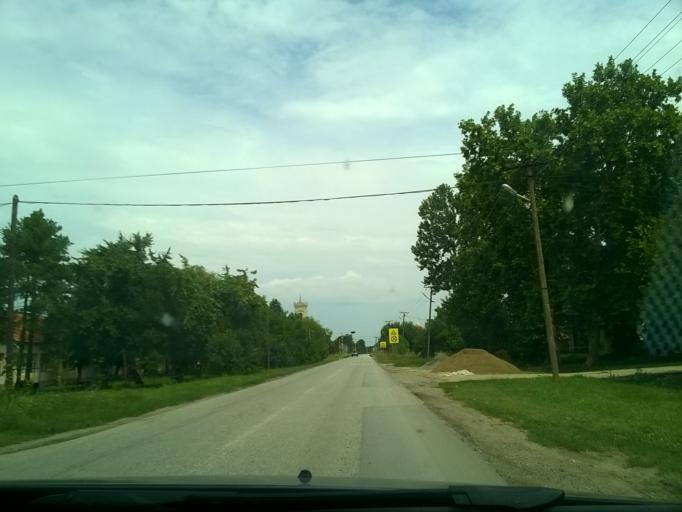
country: RS
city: Boka
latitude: 45.3543
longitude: 20.8342
